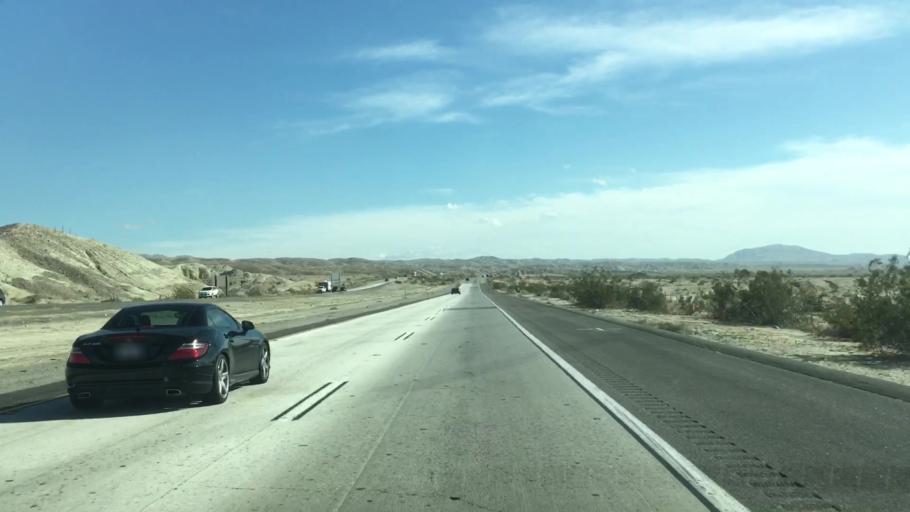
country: US
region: California
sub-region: Riverside County
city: Coachella
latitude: 33.7074
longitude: -116.1433
